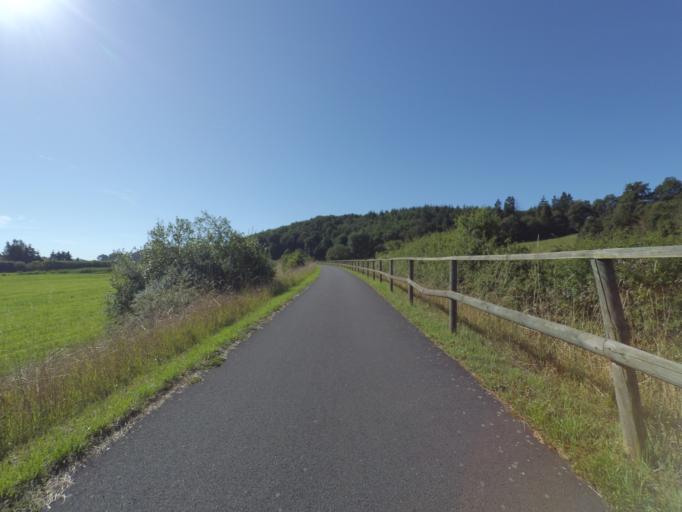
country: DE
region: Rheinland-Pfalz
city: Udler
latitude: 50.1357
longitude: 6.8876
